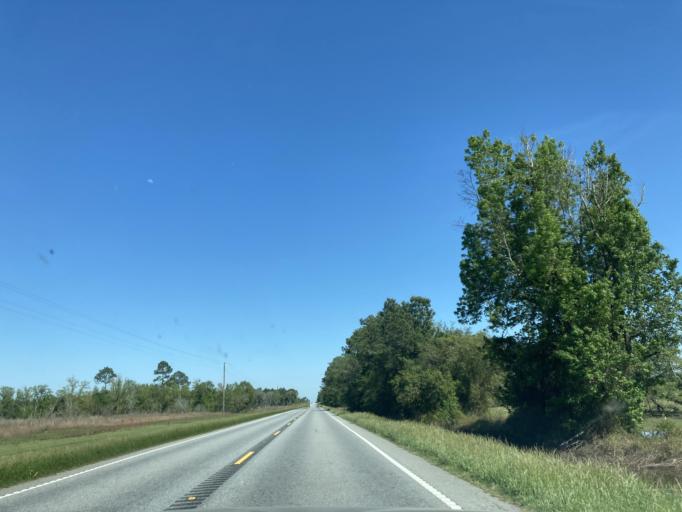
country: US
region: Georgia
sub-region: Miller County
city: Colquitt
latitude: 31.1861
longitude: -84.6246
